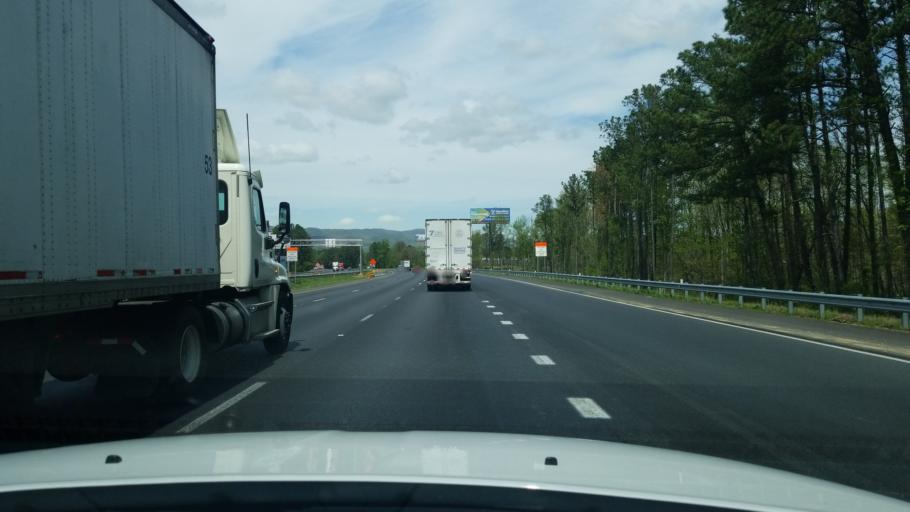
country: US
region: Georgia
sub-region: Whitfield County
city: Dalton
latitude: 34.6573
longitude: -84.9852
